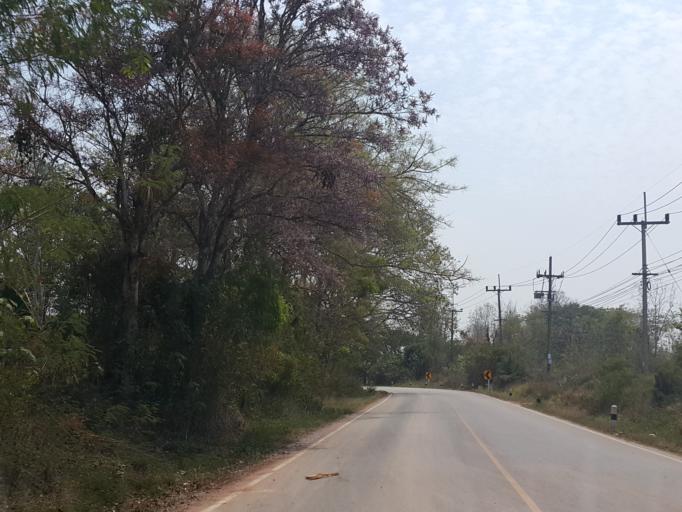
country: TH
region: Lampang
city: Chae Hom
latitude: 18.7624
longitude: 99.5556
